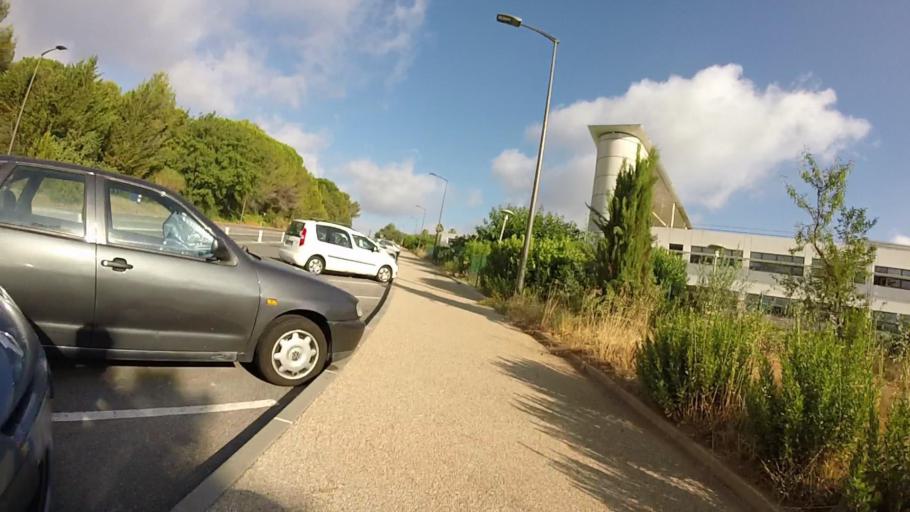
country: FR
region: Provence-Alpes-Cote d'Azur
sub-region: Departement des Alpes-Maritimes
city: Biot
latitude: 43.6233
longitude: 7.0617
